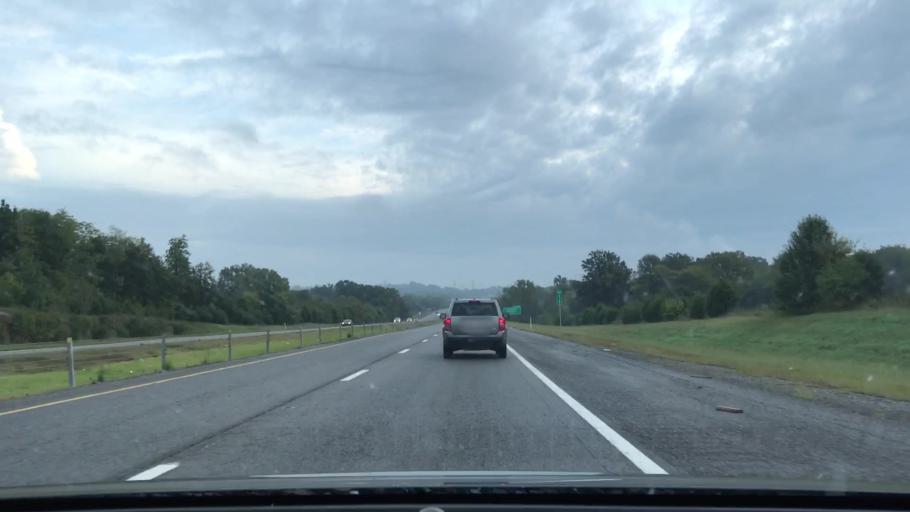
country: US
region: Tennessee
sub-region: Sumner County
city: Shackle Island
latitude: 36.3478
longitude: -86.5460
